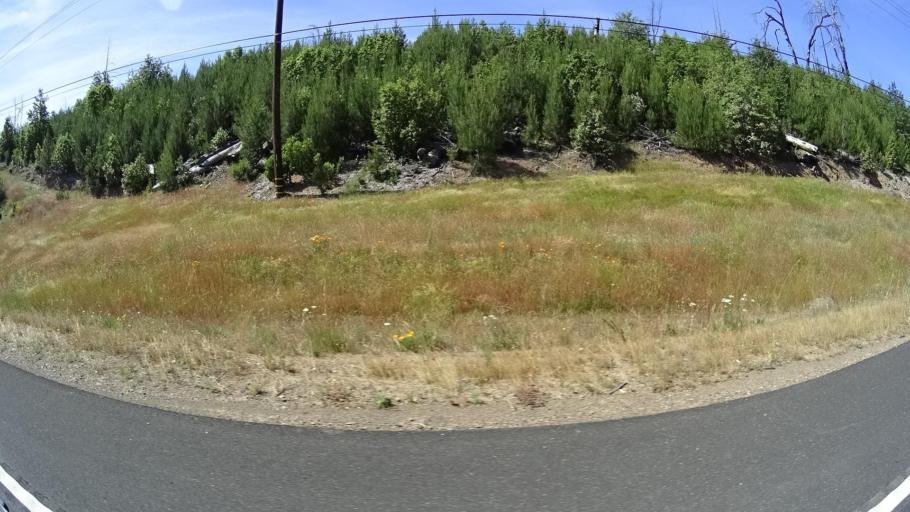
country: US
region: California
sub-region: Lake County
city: Middletown
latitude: 38.7666
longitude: -122.6536
